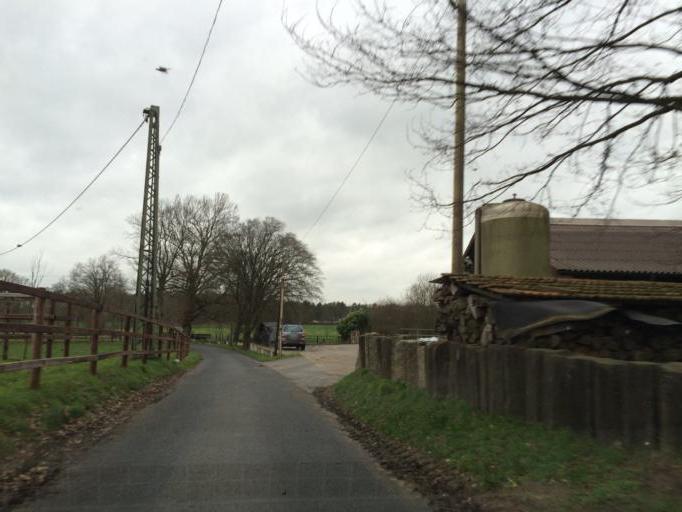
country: DE
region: North Rhine-Westphalia
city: Marl
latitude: 51.7031
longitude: 7.0733
